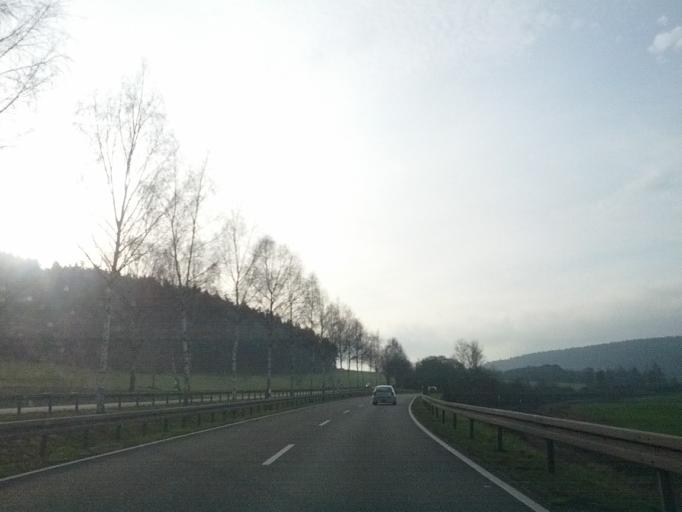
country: DE
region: Thuringia
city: Wallbach
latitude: 50.6387
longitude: 10.3809
